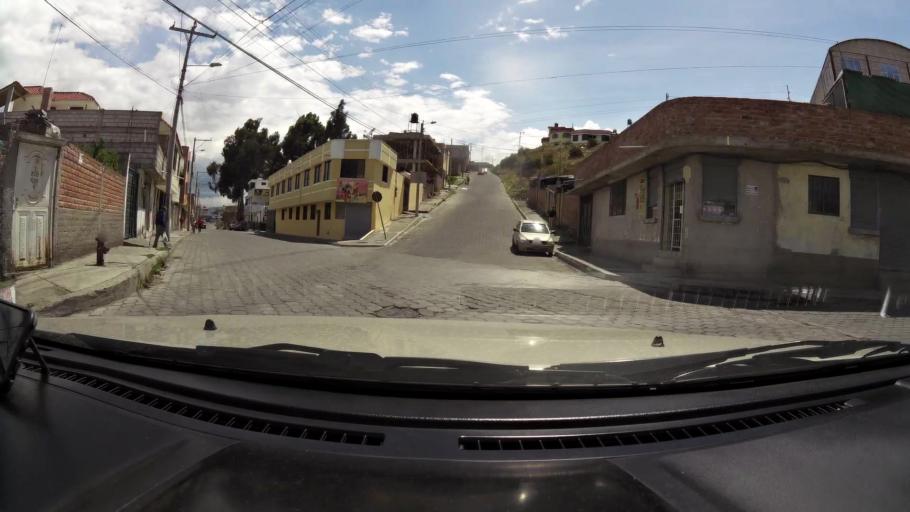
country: EC
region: Chimborazo
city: Riobamba
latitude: -1.6588
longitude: -78.6415
